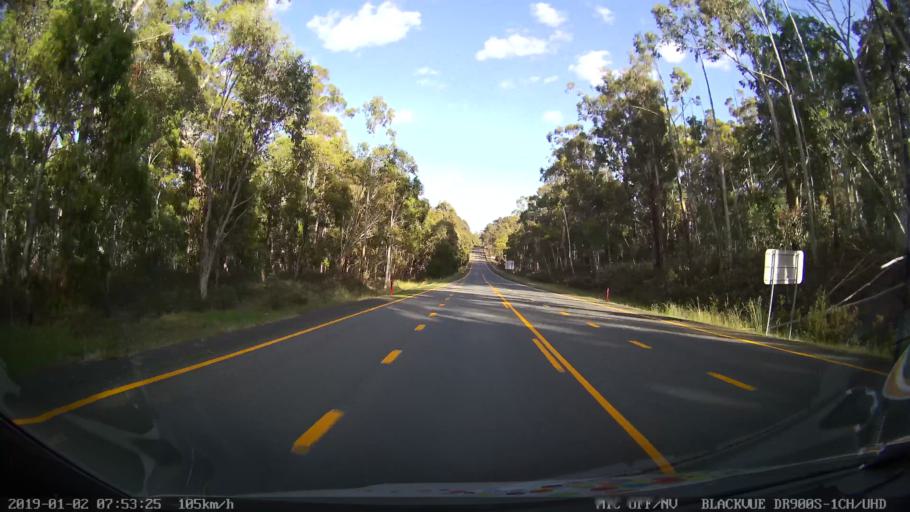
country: AU
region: New South Wales
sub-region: Tumut Shire
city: Tumut
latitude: -35.7056
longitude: 148.5067
